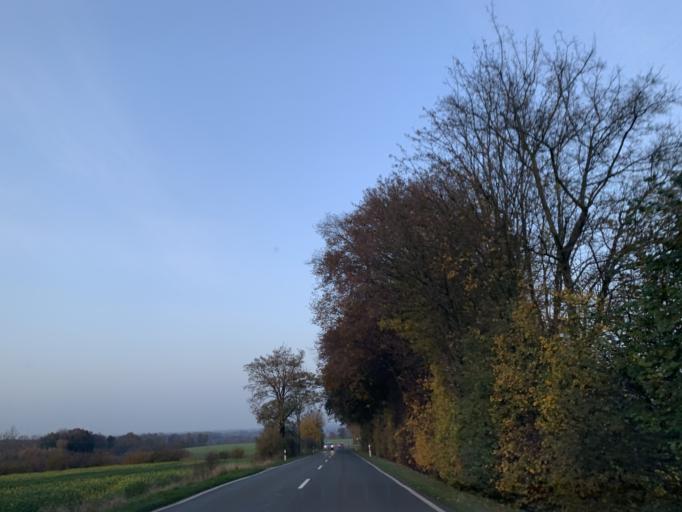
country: DE
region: North Rhine-Westphalia
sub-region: Regierungsbezirk Munster
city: Nottuln
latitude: 51.9774
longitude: 7.3521
